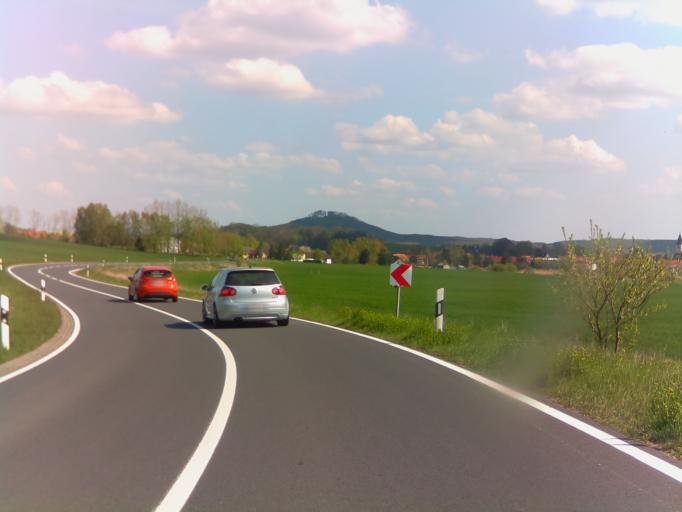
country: DE
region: Thuringia
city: Westhausen
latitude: 50.3624
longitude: 10.6742
